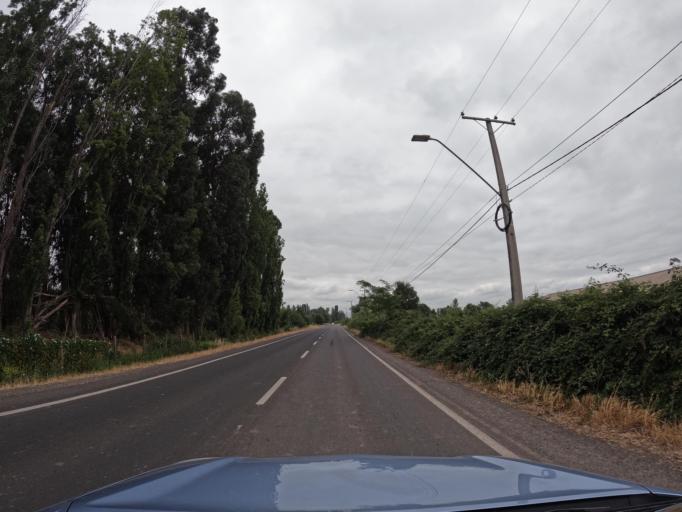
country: CL
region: O'Higgins
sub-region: Provincia de Colchagua
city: Chimbarongo
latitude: -34.7314
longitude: -71.0739
